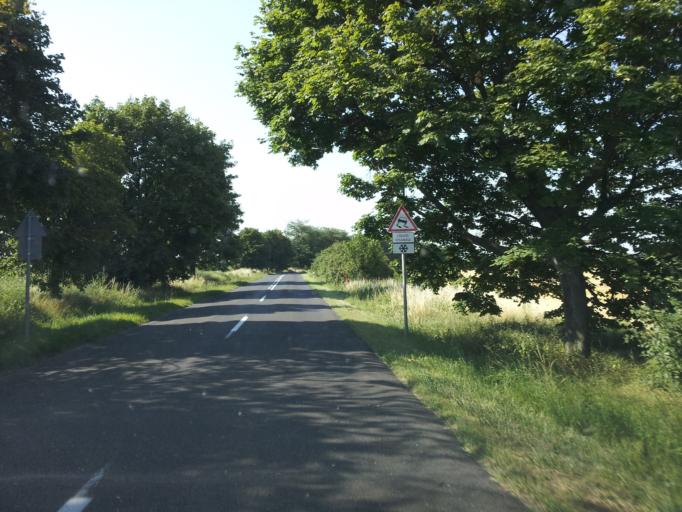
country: HU
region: Fejer
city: Lovasbereny
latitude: 47.3876
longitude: 18.5866
